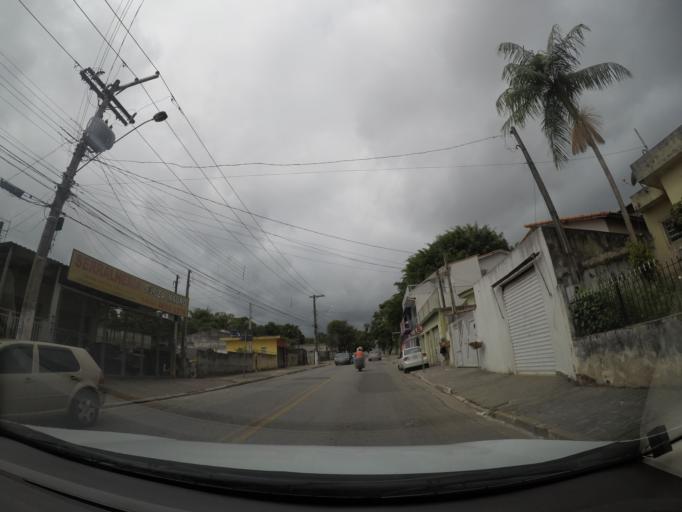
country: BR
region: Sao Paulo
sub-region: Aruja
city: Aruja
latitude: -23.3926
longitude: -46.3138
